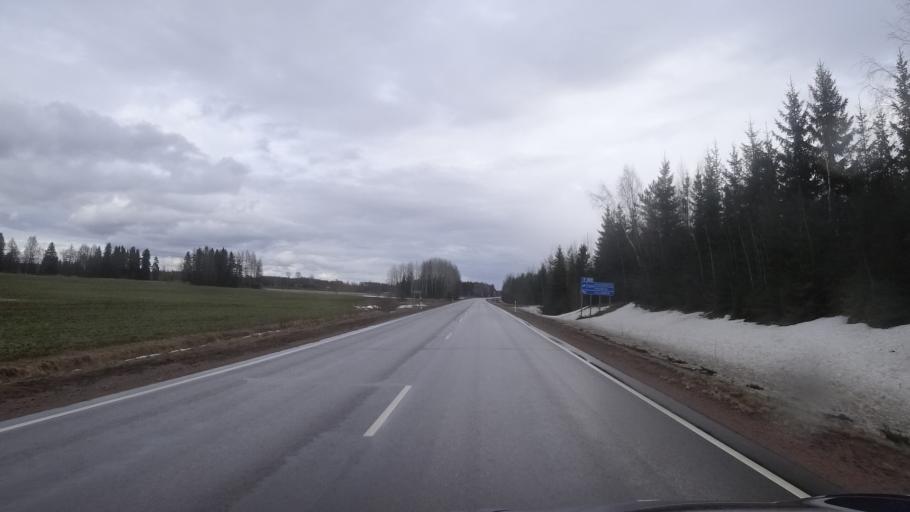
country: FI
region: Kymenlaakso
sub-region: Kouvola
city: Elimaeki
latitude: 60.6908
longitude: 26.5620
